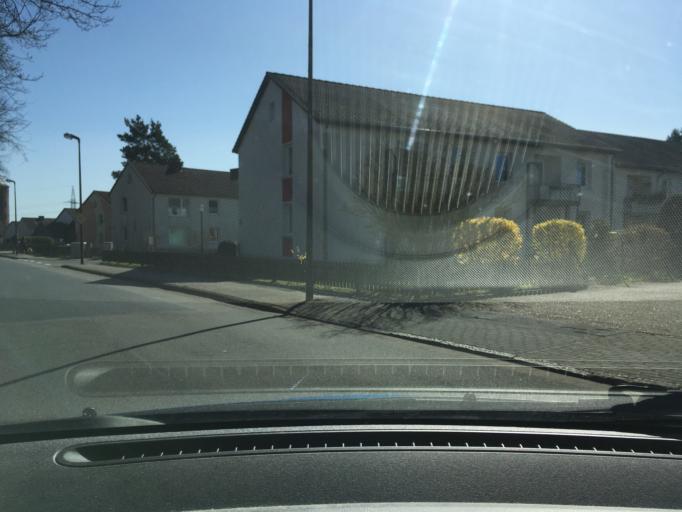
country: DE
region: Lower Saxony
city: Uelzen
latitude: 52.9643
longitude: 10.5371
